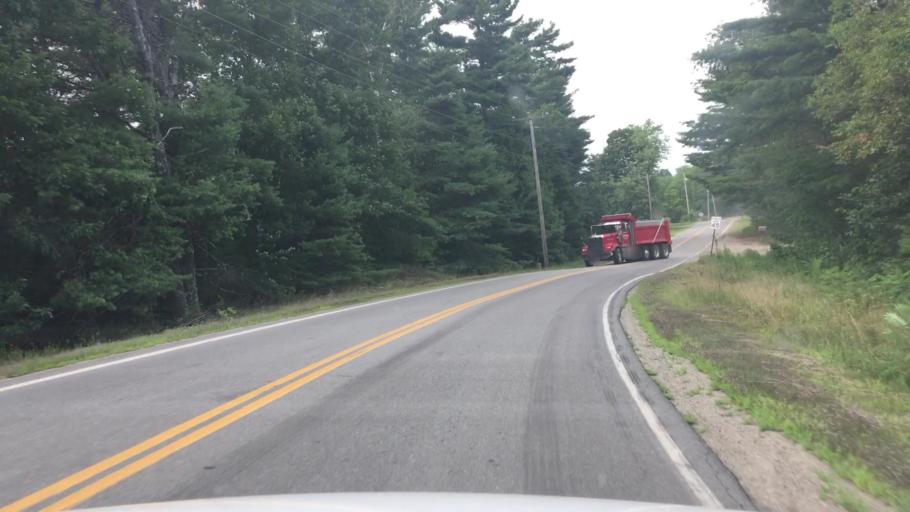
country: US
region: Maine
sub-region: Knox County
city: Washington
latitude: 44.2284
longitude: -69.3882
